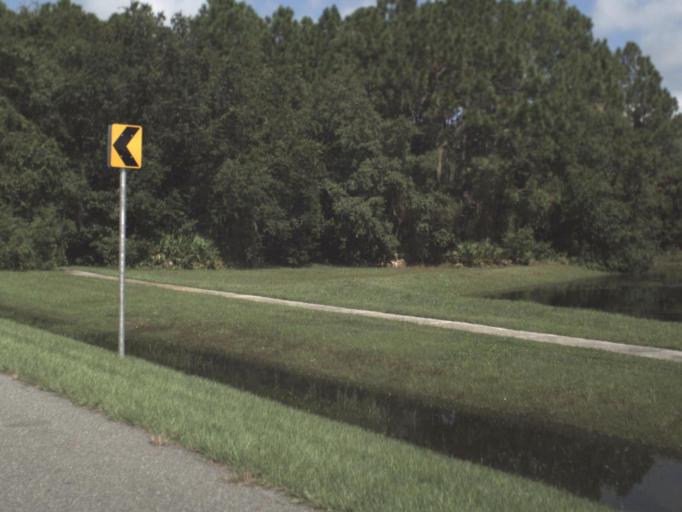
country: US
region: Florida
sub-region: Sarasota County
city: Lake Sarasota
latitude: 27.2687
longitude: -82.4191
